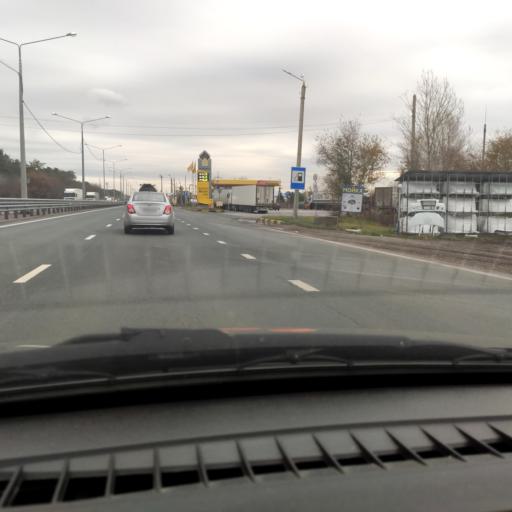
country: RU
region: Samara
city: Zhigulevsk
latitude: 53.5135
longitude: 49.6014
